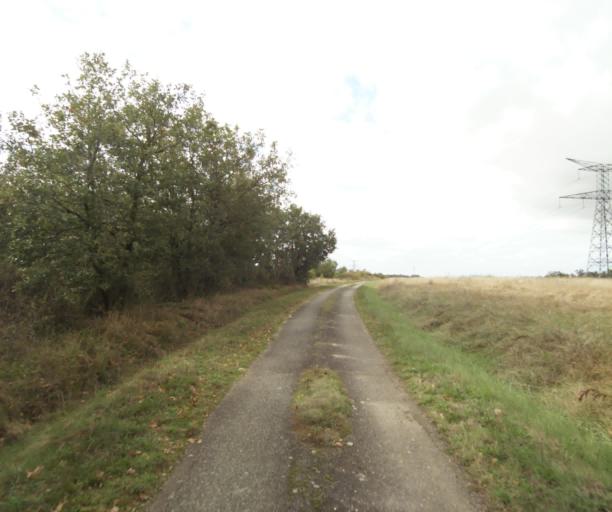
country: FR
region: Midi-Pyrenees
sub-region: Departement du Tarn-et-Garonne
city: Beaumont-de-Lomagne
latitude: 43.9083
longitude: 1.1020
